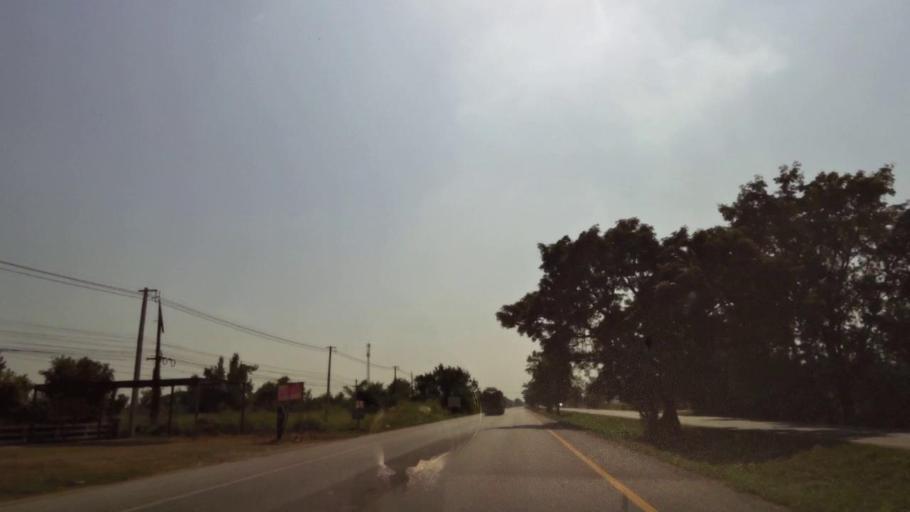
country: TH
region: Phichit
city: Bueng Na Rang
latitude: 16.3102
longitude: 100.1286
